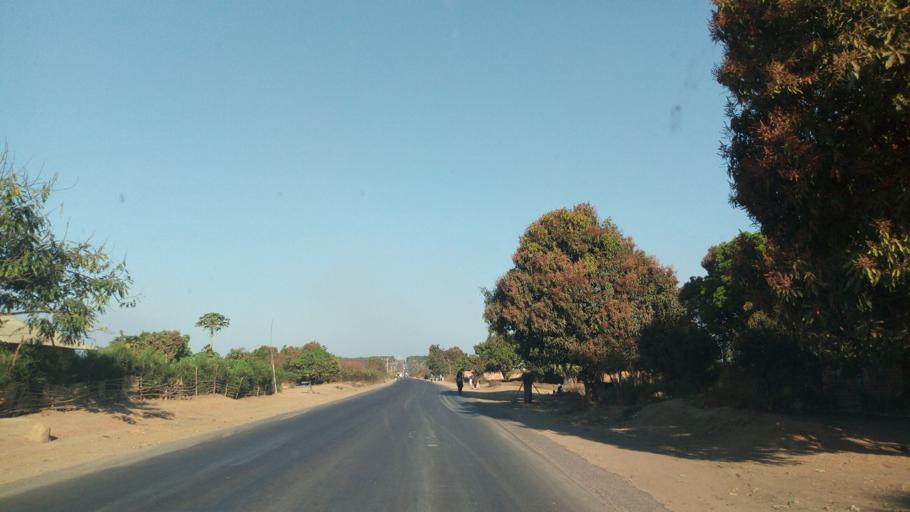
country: CD
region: Katanga
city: Likasi
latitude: -11.0486
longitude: 26.9551
